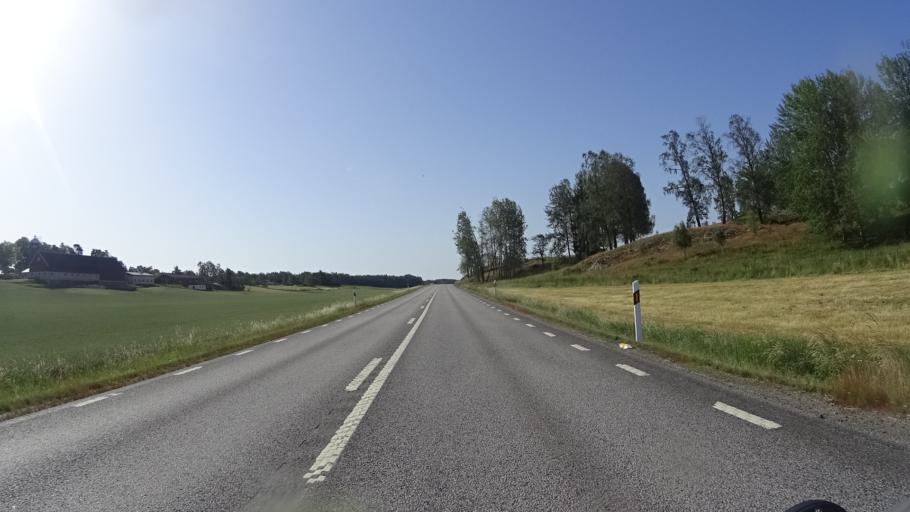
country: SE
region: OEstergoetland
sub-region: Linkopings Kommun
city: Linghem
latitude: 58.3488
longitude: 15.8391
